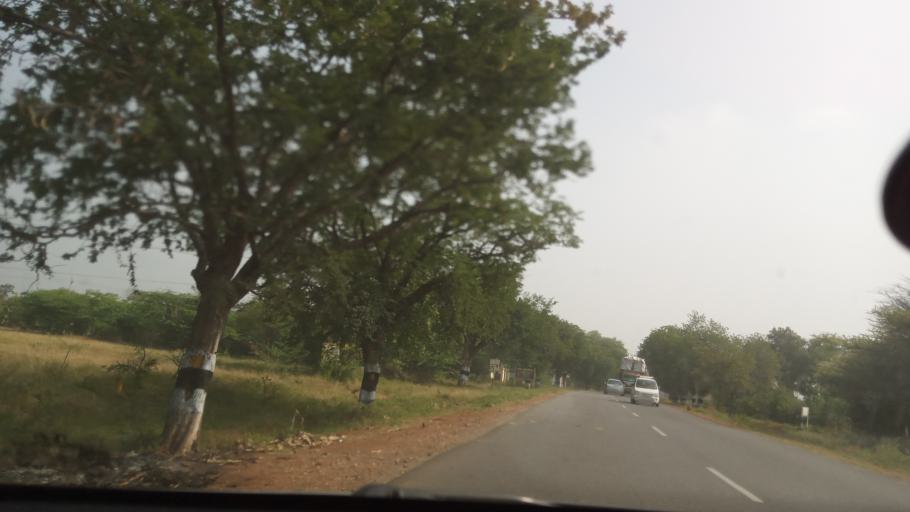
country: IN
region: Tamil Nadu
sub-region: Erode
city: Sathyamangalam
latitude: 11.4310
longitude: 77.2000
